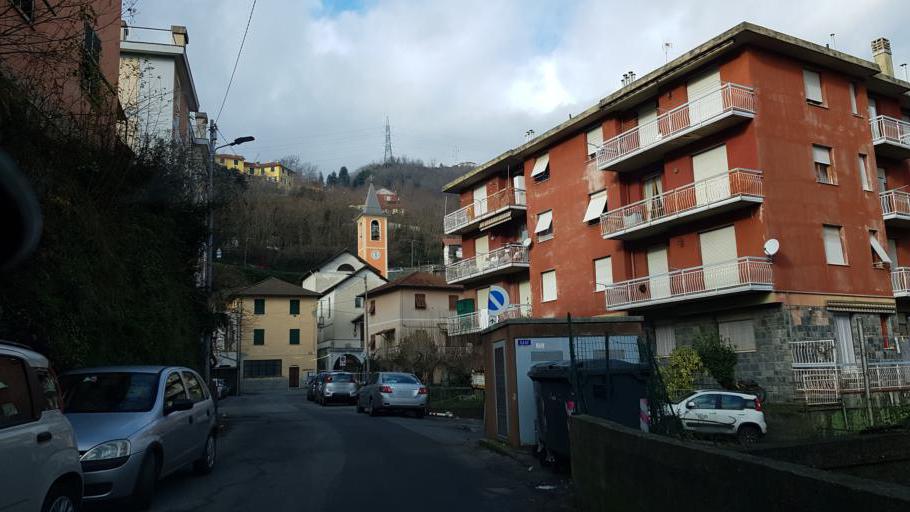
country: IT
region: Liguria
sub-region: Provincia di Genova
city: Santa Marta
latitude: 44.4744
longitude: 8.8884
